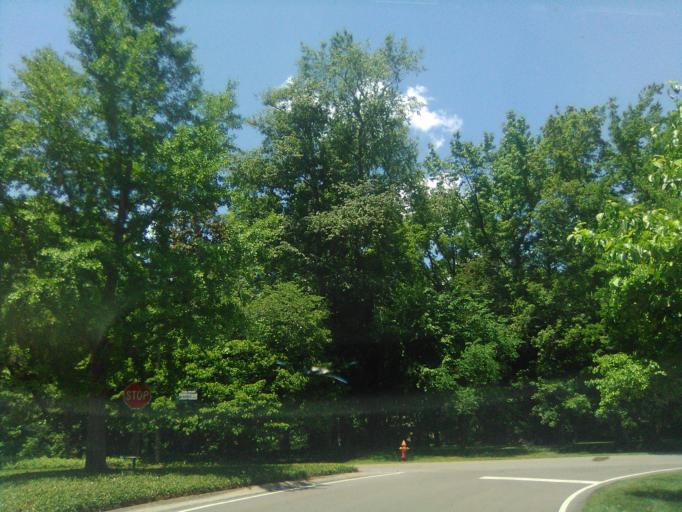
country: US
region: Tennessee
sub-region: Davidson County
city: Belle Meade
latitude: 36.1138
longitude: -86.8567
